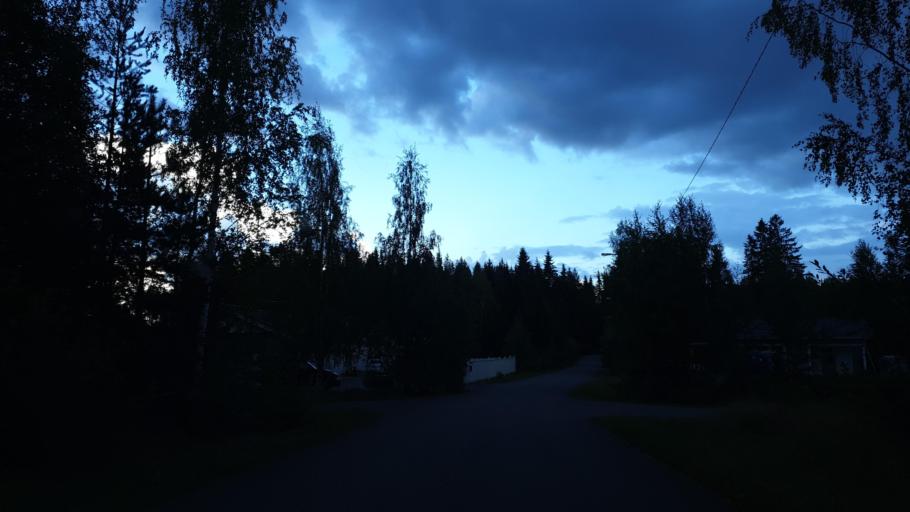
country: FI
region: Northern Savo
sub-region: Varkaus
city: Leppaevirta
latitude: 62.5834
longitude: 27.6209
